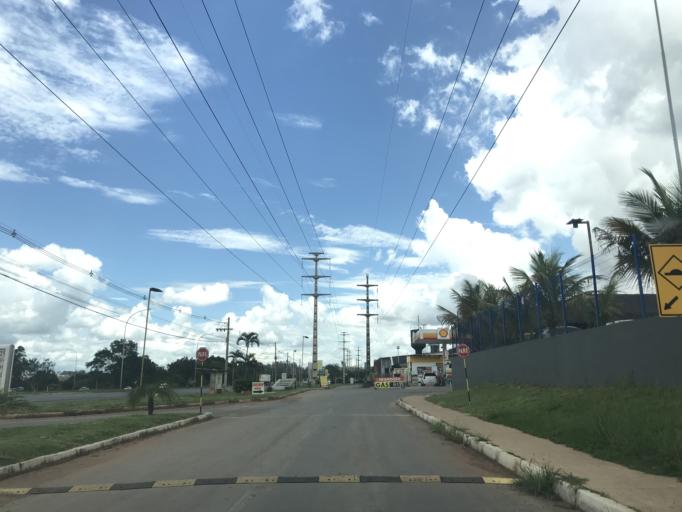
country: BR
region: Federal District
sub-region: Brasilia
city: Brasilia
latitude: -15.8748
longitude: -48.0317
